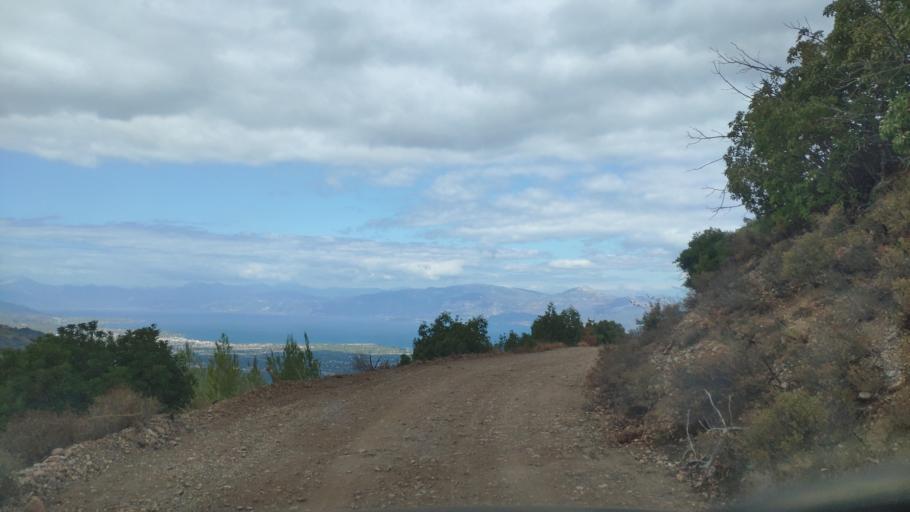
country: GR
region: West Greece
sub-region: Nomos Achaias
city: Temeni
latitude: 38.1743
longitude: 22.1551
